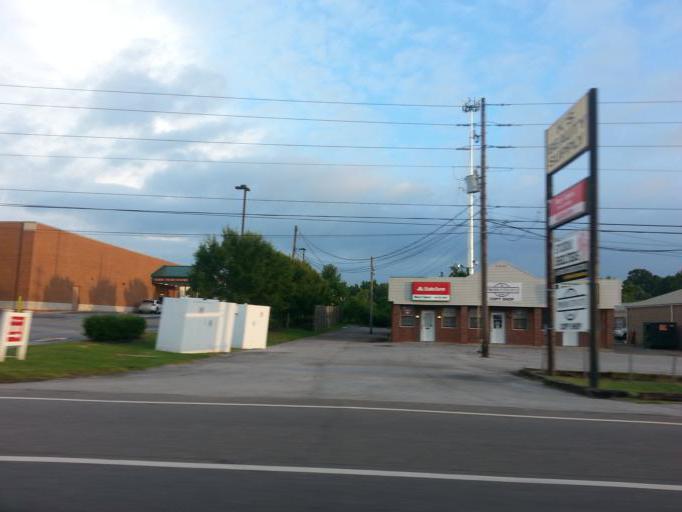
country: US
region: Alabama
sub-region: Madison County
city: Madison
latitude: 34.7535
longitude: -86.7425
